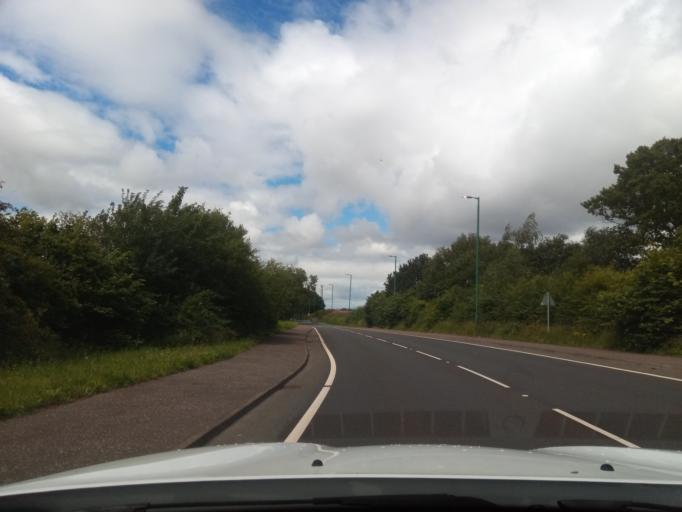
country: GB
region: Scotland
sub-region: Fife
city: Kincardine
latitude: 56.0660
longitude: -3.7029
